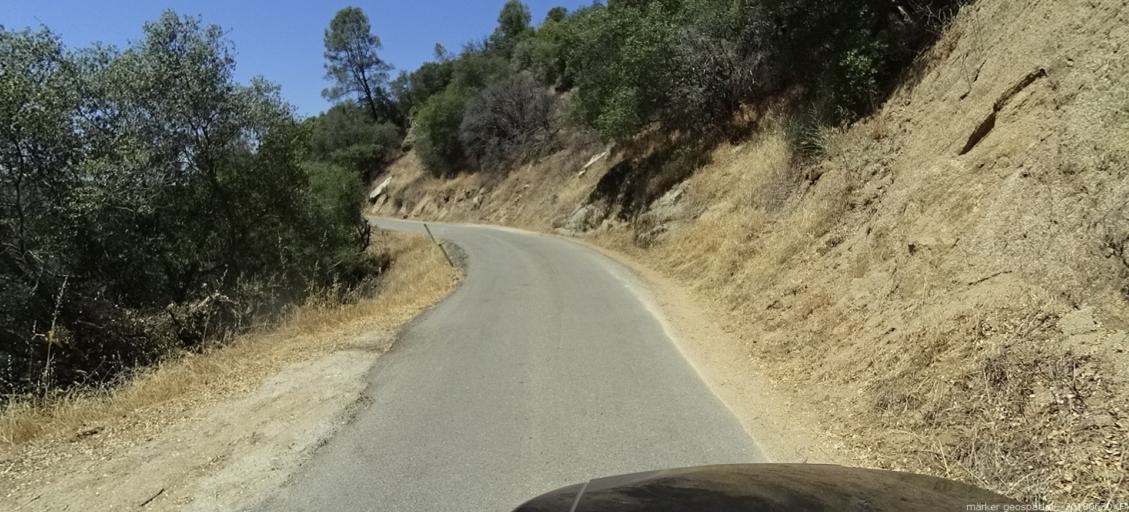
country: US
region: California
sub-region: Fresno County
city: Auberry
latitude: 37.1636
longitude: -119.4465
